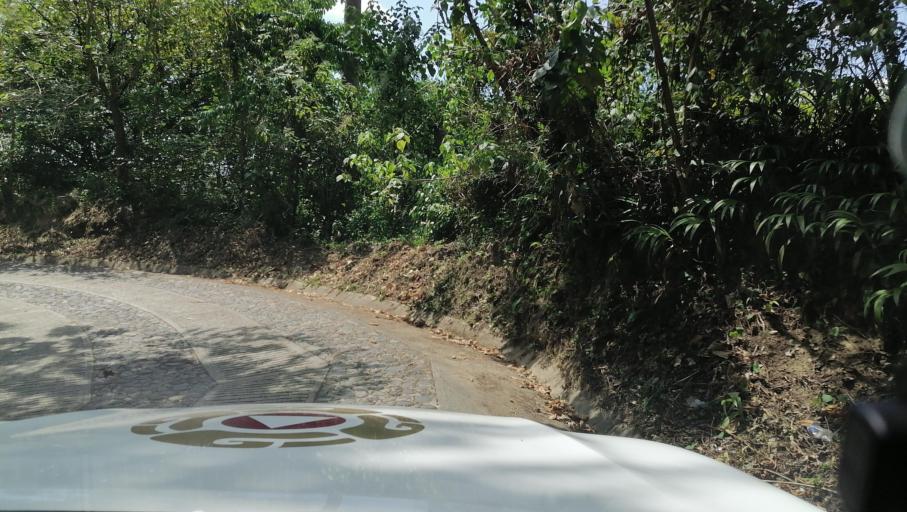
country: MX
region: Chiapas
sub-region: Tapachula
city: Canton Villaflor
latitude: 15.1354
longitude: -92.2919
